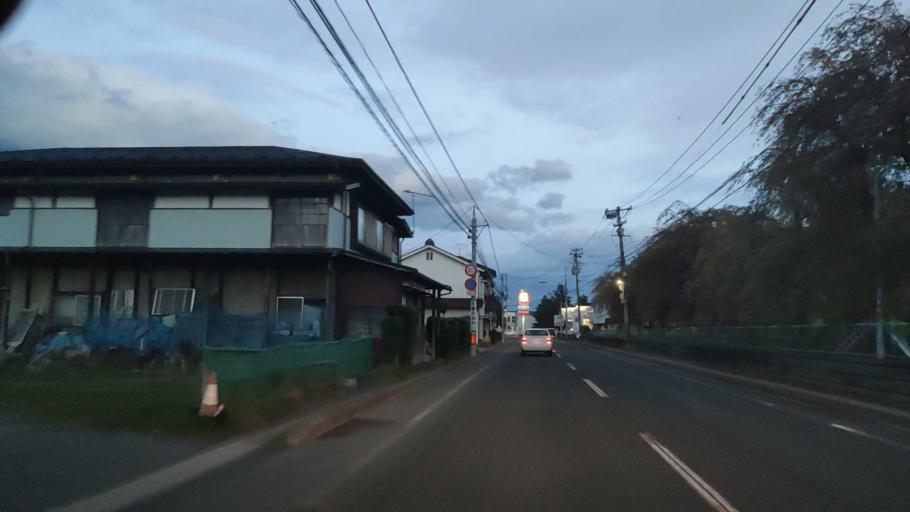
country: JP
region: Iwate
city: Morioka-shi
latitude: 39.7182
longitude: 141.1226
